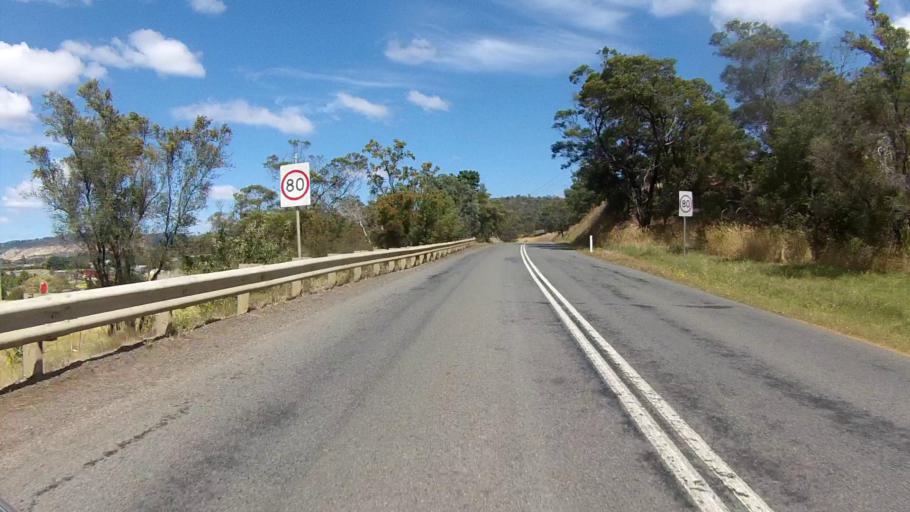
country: AU
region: Tasmania
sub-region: Clarence
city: Cambridge
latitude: -42.6569
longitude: 147.4297
